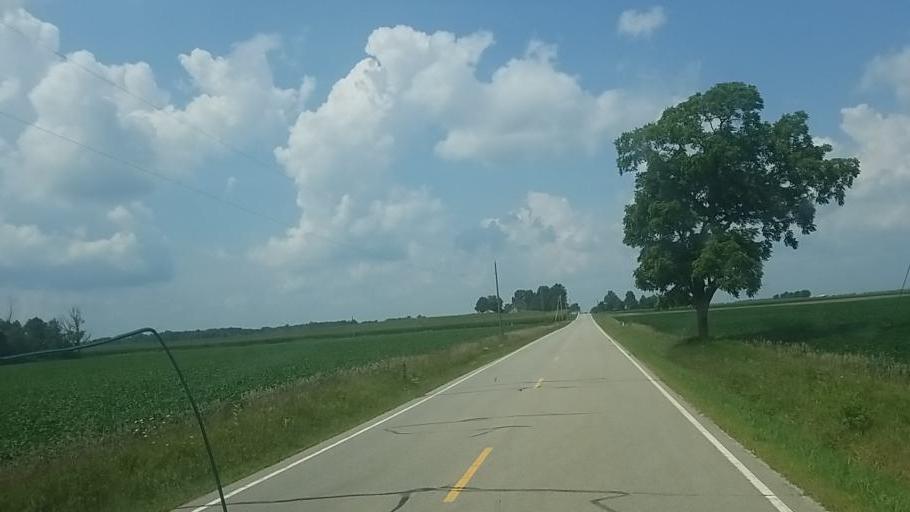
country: US
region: Ohio
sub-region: Crawford County
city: Galion
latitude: 40.7986
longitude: -82.8701
